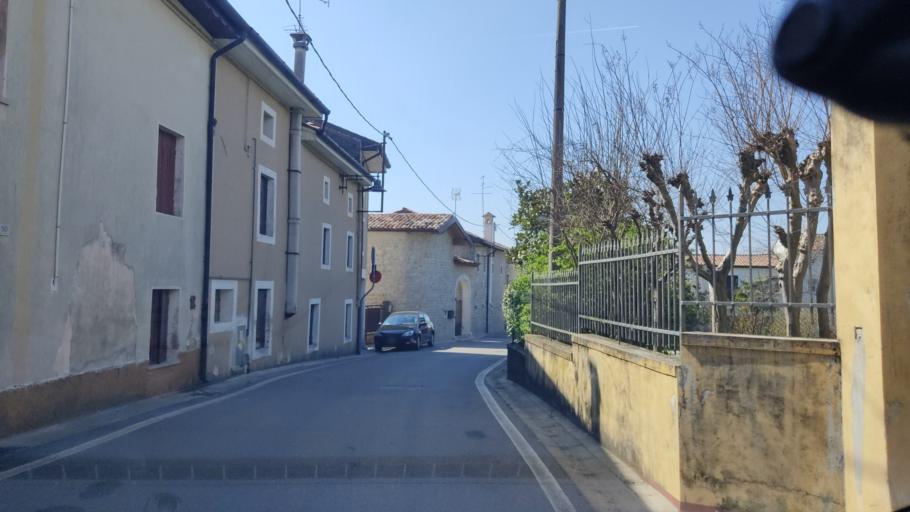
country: IT
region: Friuli Venezia Giulia
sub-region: Provincia di Pordenone
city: Budoia
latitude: 46.0468
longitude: 12.5315
